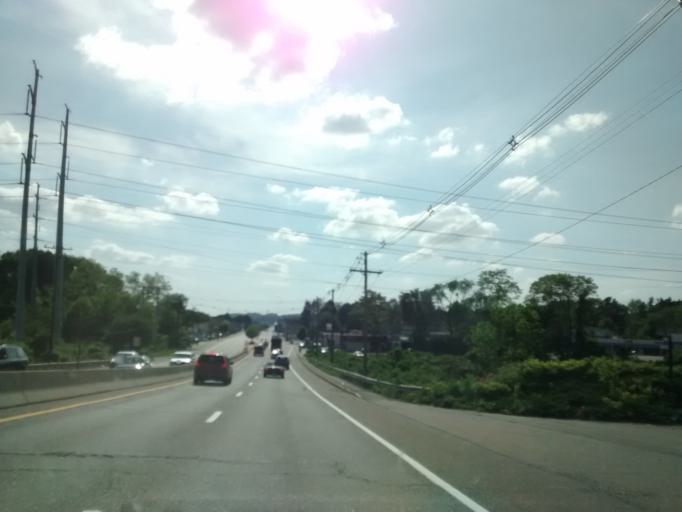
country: US
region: Massachusetts
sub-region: Worcester County
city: Shrewsbury
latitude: 42.2760
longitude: -71.7343
